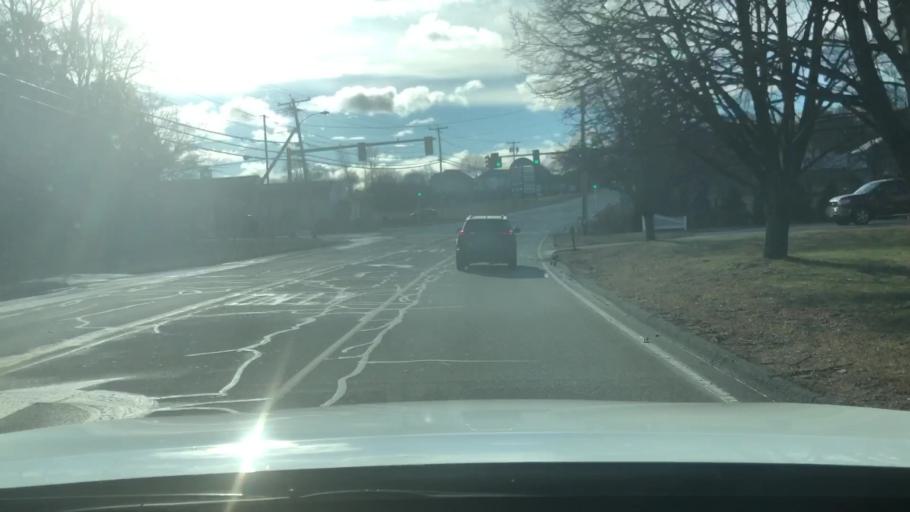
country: US
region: Massachusetts
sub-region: Norfolk County
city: Bellingham
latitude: 42.0533
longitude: -71.4845
